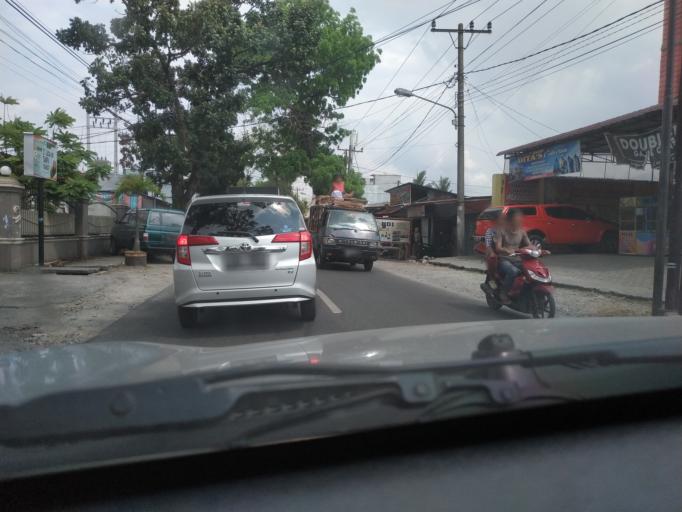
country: ID
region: North Sumatra
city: Sunggal
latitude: 3.5847
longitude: 98.6297
